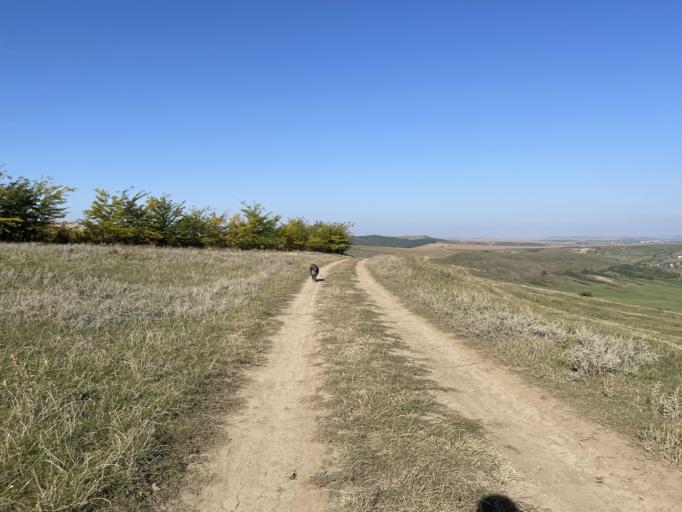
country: RO
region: Iasi
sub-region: Comuna Dumesti
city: Pausesti
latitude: 47.1502
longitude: 27.3123
